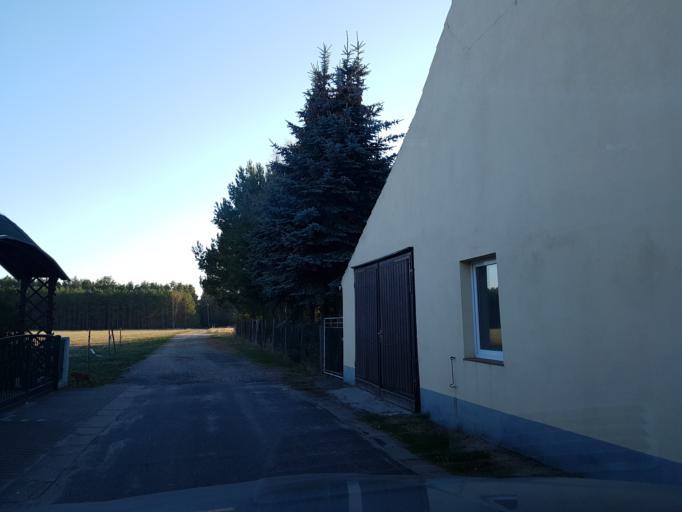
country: DE
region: Brandenburg
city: Bad Liebenwerda
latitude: 51.5466
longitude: 13.3843
